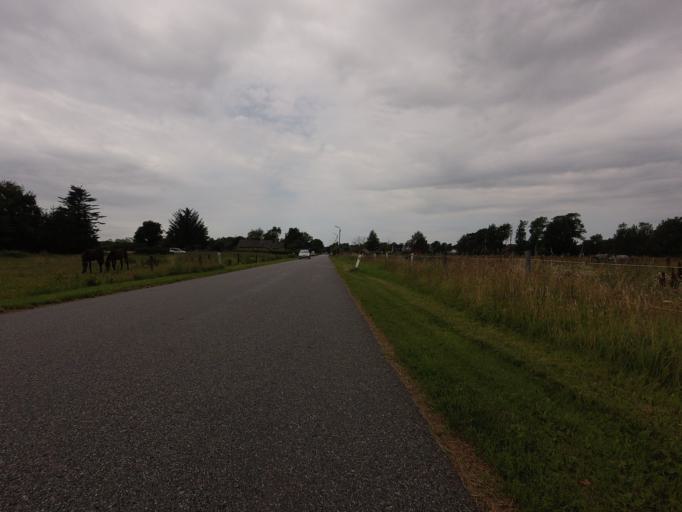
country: DK
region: North Denmark
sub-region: Alborg Kommune
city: Vadum
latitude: 57.1133
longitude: 9.8656
